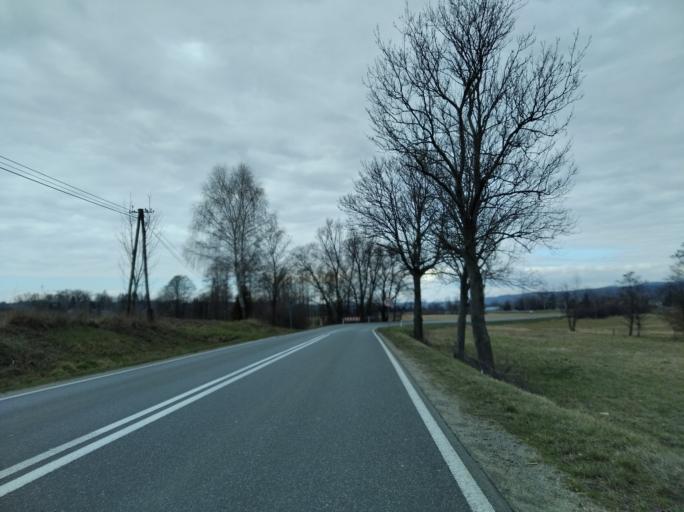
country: PL
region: Subcarpathian Voivodeship
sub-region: Powiat krosnienski
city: Wojaszowka
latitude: 49.7880
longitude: 21.6601
